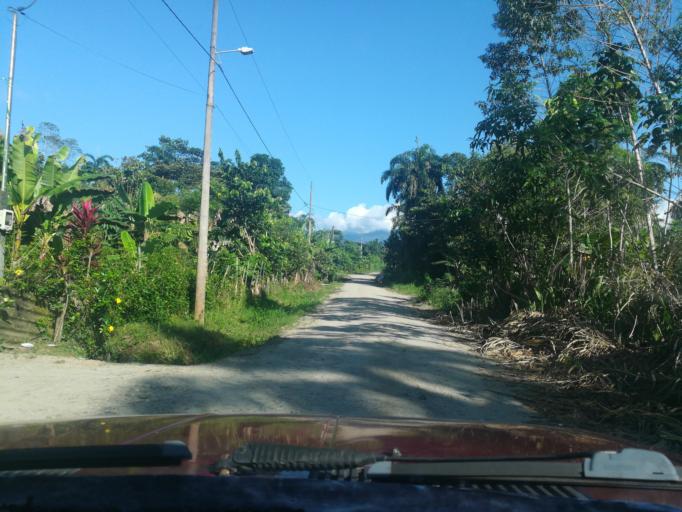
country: EC
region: Napo
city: Tena
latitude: -0.9924
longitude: -77.8313
